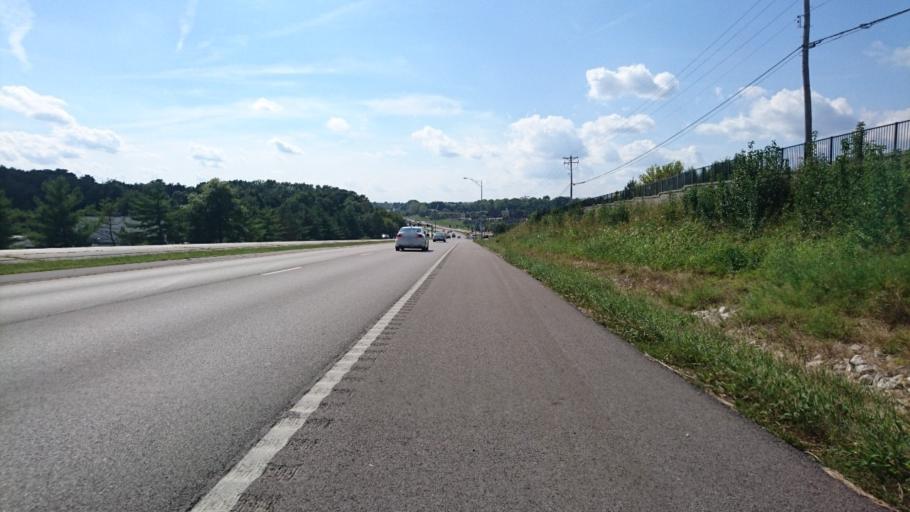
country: US
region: Missouri
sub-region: Saint Louis County
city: Ellisville
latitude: 38.5883
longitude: -90.6044
